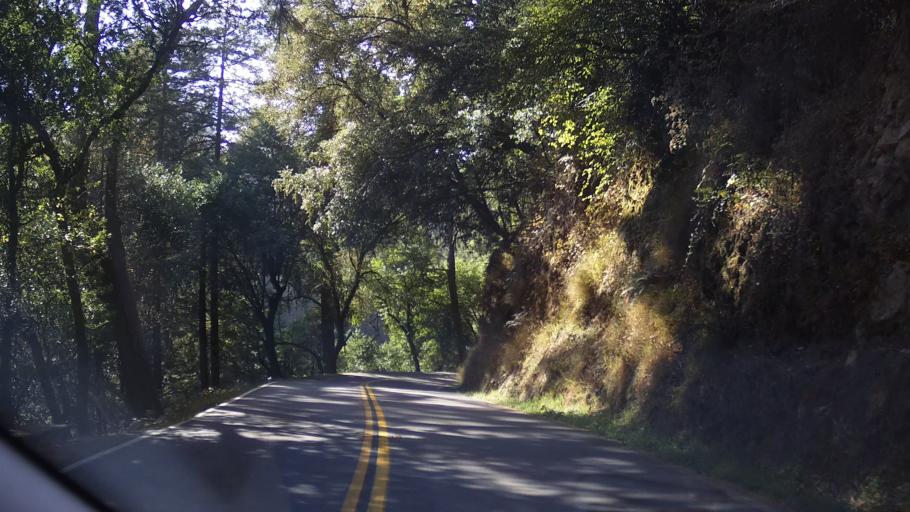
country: US
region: California
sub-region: Marin County
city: Mill Valley
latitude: 37.8977
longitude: -122.6130
